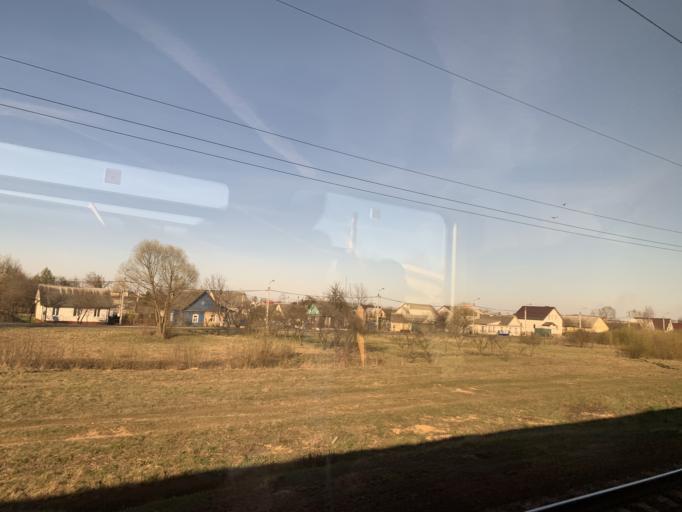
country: BY
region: Minsk
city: Maladzyechna
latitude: 54.3127
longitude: 26.8573
